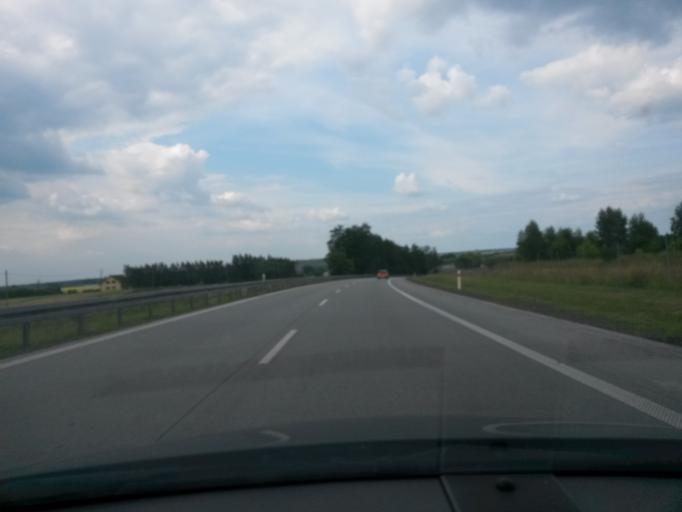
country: PL
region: Lodz Voivodeship
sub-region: Powiat skierniewicki
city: Kowiesy
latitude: 51.8745
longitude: 20.3877
